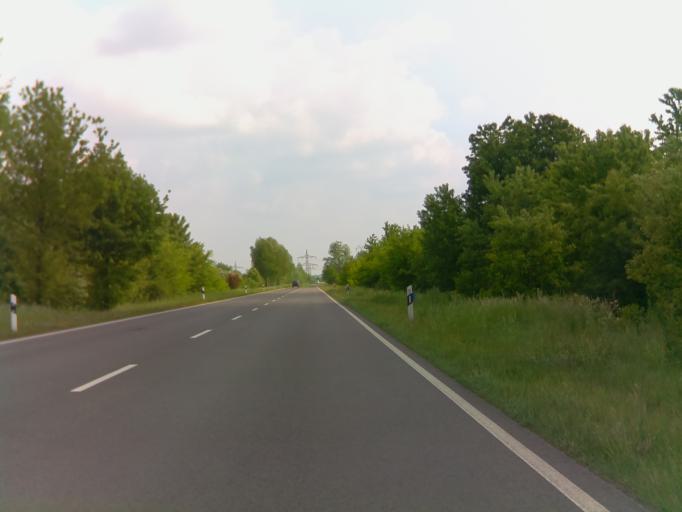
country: DE
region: Saxony-Anhalt
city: Gardelegen
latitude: 52.5279
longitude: 11.3620
